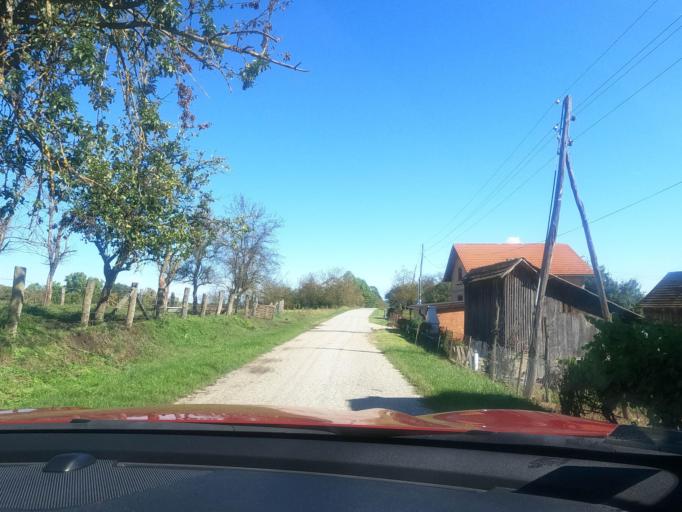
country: HR
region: Sisacko-Moslavacka
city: Glina
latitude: 45.3381
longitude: 16.2099
